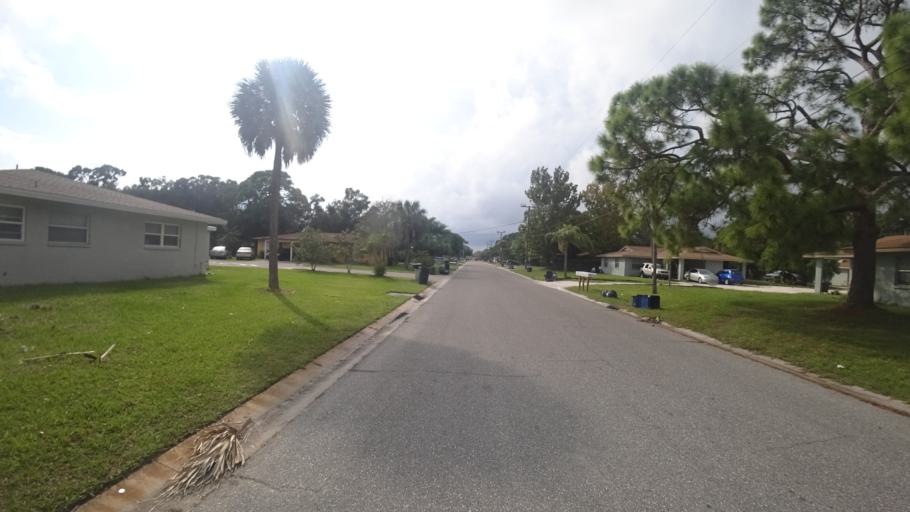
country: US
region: Florida
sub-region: Manatee County
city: Whitfield
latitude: 27.4237
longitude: -82.5717
